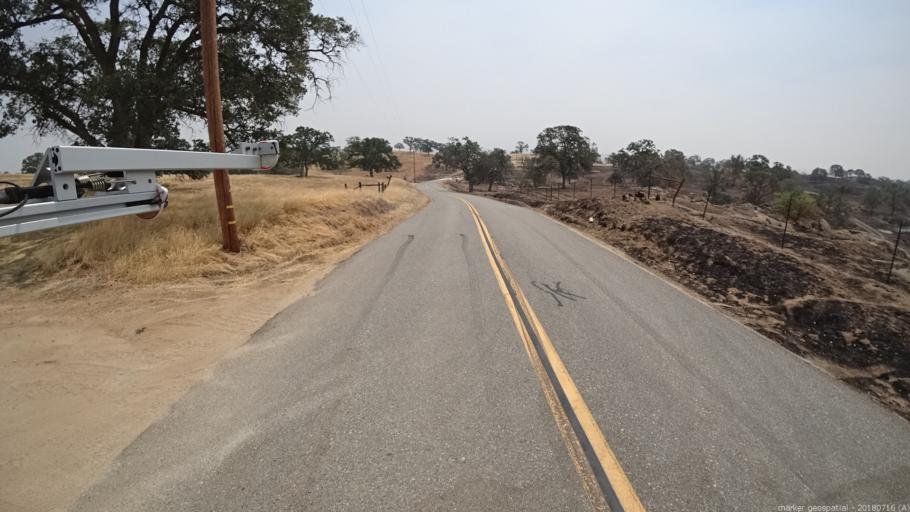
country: US
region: California
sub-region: Madera County
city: Yosemite Lakes
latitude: 37.1483
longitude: -119.9120
